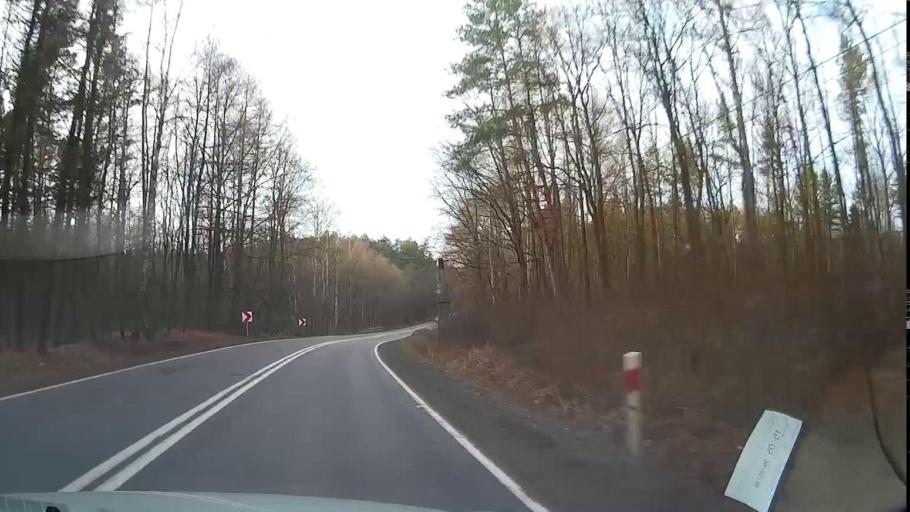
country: PL
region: Lesser Poland Voivodeship
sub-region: Powiat chrzanowski
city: Brodla
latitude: 50.0340
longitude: 19.6078
